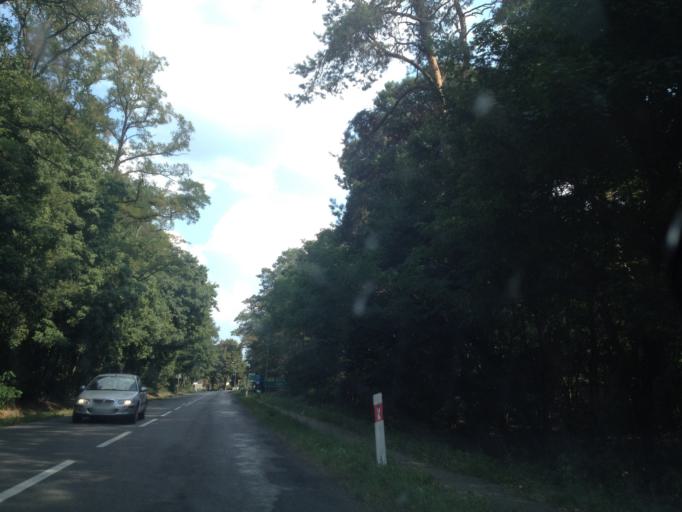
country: PL
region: Greater Poland Voivodeship
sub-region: Powiat poznanski
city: Rogalinek
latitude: 52.2306
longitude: 16.9446
